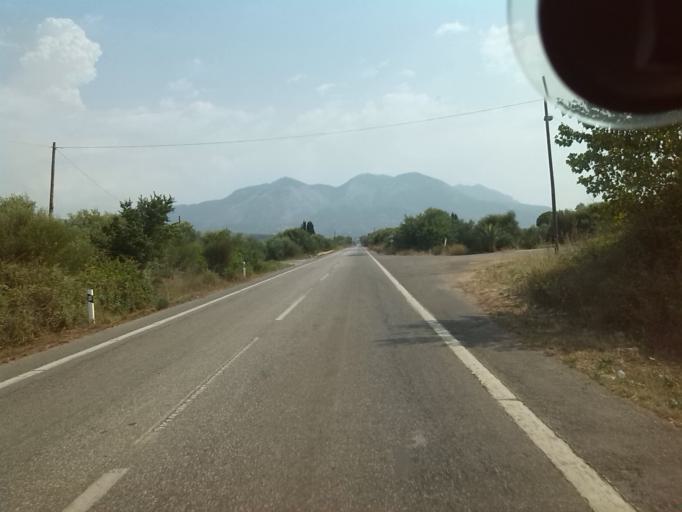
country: GR
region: Peloponnese
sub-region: Nomos Messinias
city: Kyparissia
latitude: 37.3113
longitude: 21.7023
